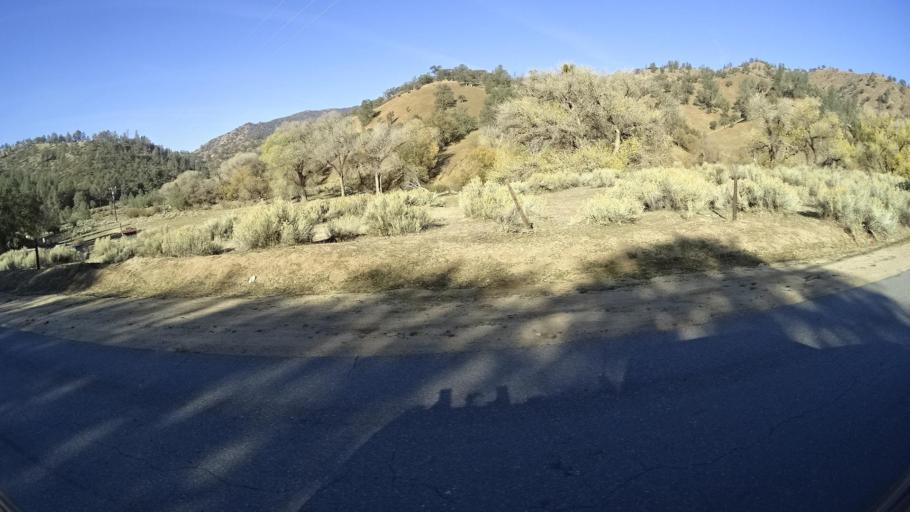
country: US
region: California
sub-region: Kern County
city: Golden Hills
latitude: 35.3050
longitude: -118.4349
